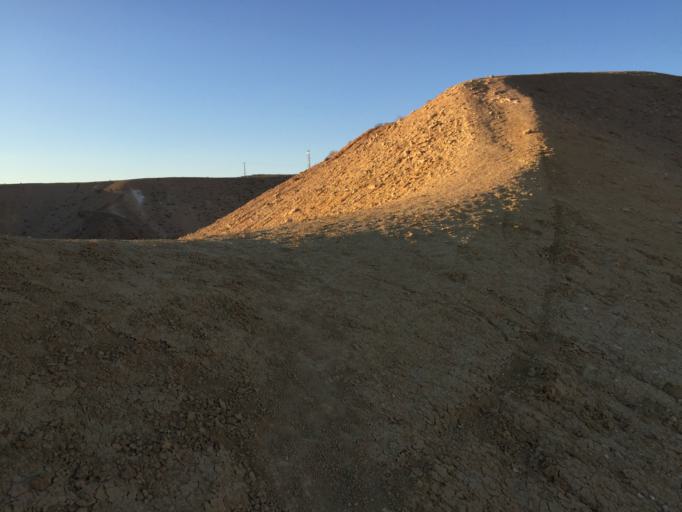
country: IL
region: Southern District
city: Midreshet Ben-Gurion
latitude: 30.8453
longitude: 34.7556
